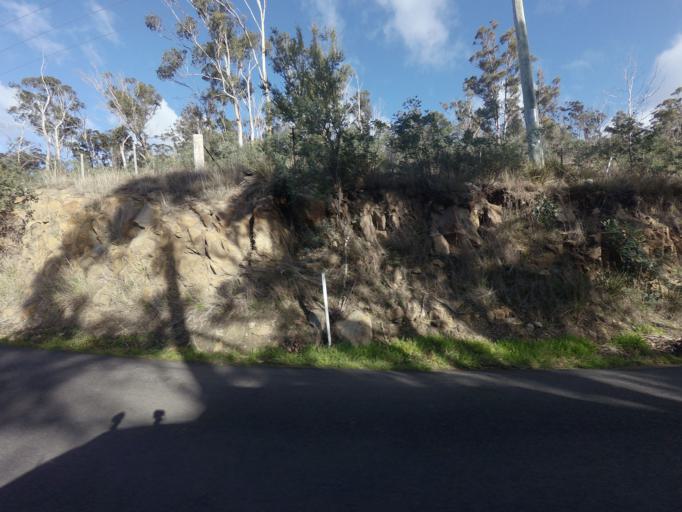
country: AU
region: Tasmania
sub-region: Derwent Valley
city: New Norfolk
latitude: -42.8036
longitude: 147.1496
